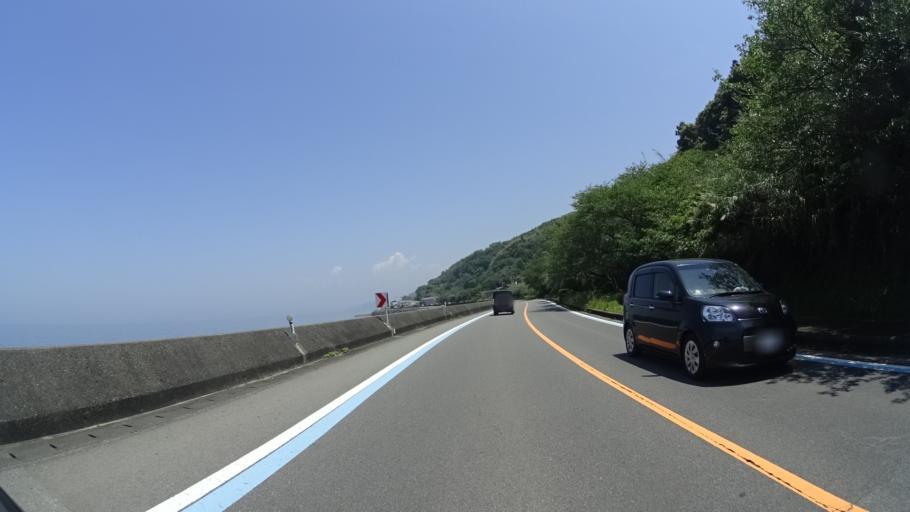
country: JP
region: Ehime
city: Iyo
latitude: 33.6544
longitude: 132.5871
